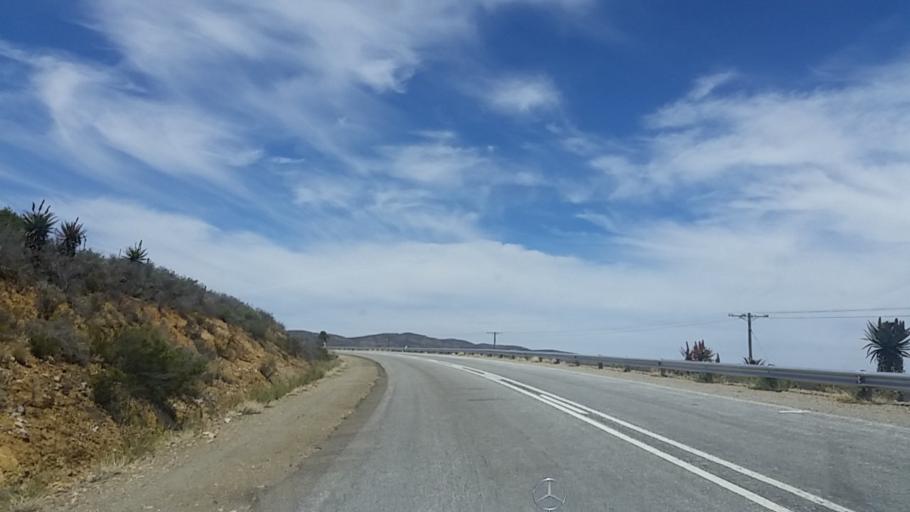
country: ZA
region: Western Cape
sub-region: Eden District Municipality
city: Knysna
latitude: -33.6311
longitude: 23.1275
